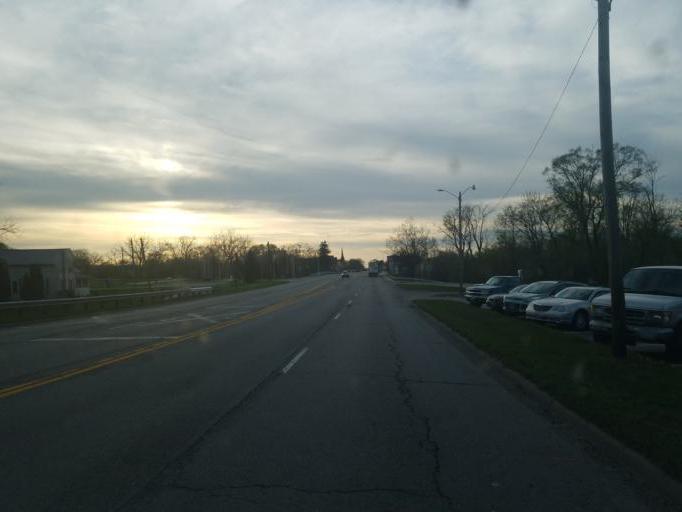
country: US
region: Ohio
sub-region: Sandusky County
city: Woodville
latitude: 41.4486
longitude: -83.3584
